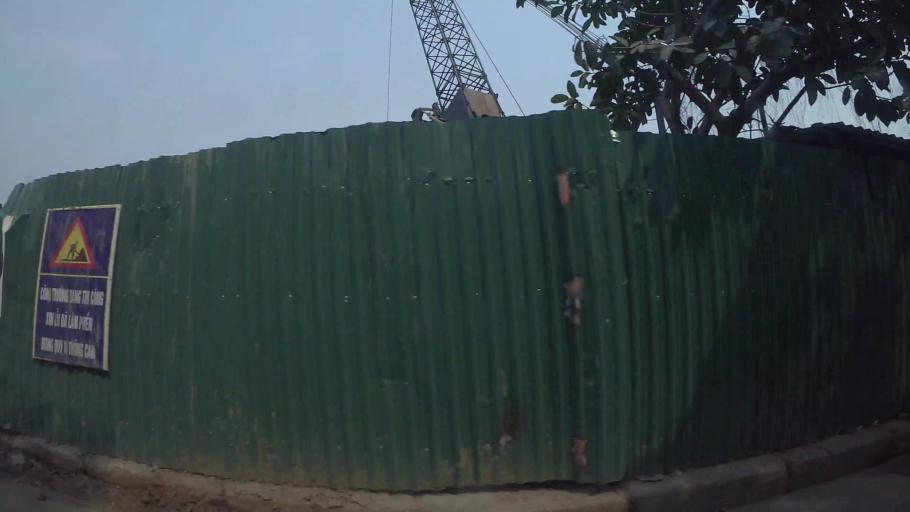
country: VN
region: Ha Noi
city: Van Dien
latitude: 20.9663
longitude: 105.8225
